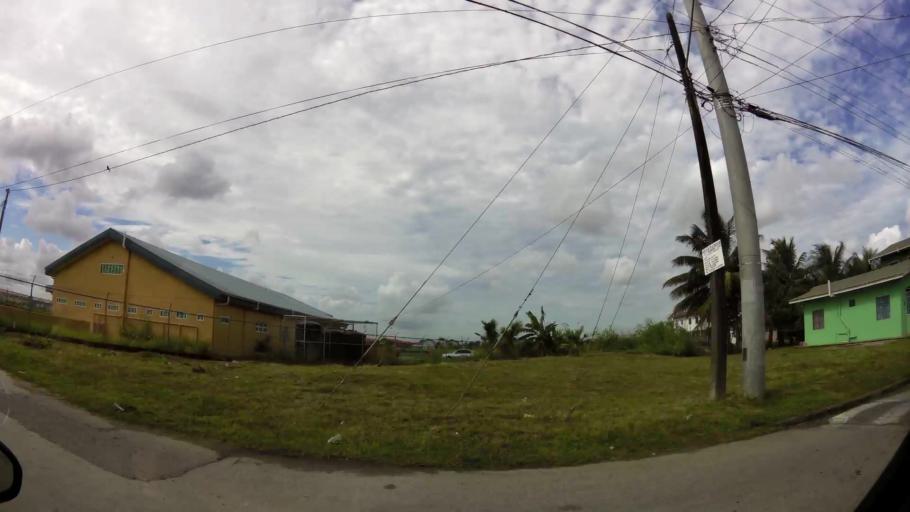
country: TT
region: Chaguanas
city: Chaguanas
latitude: 10.5065
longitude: -61.3968
